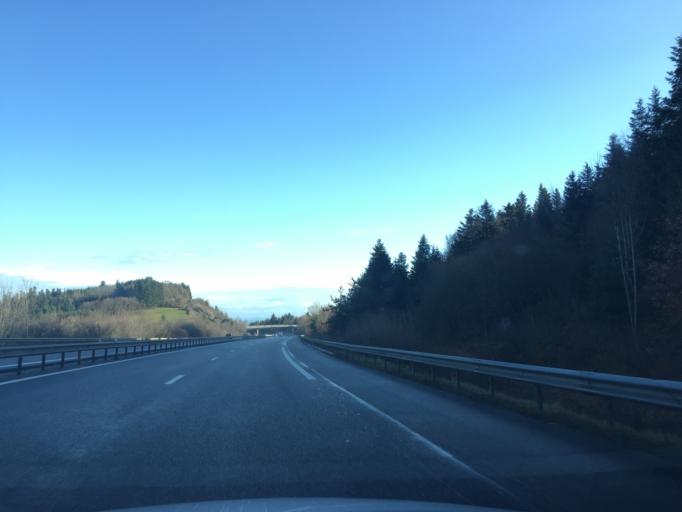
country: FR
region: Rhone-Alpes
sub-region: Departement de la Loire
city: Saint-Just-en-Chevalet
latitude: 45.8784
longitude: 3.8747
